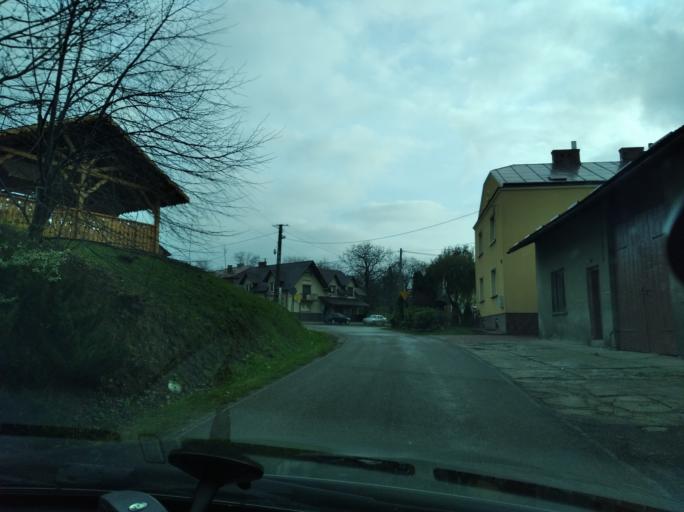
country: PL
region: Subcarpathian Voivodeship
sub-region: Powiat przeworski
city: Sietesz
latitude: 49.9997
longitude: 22.3548
